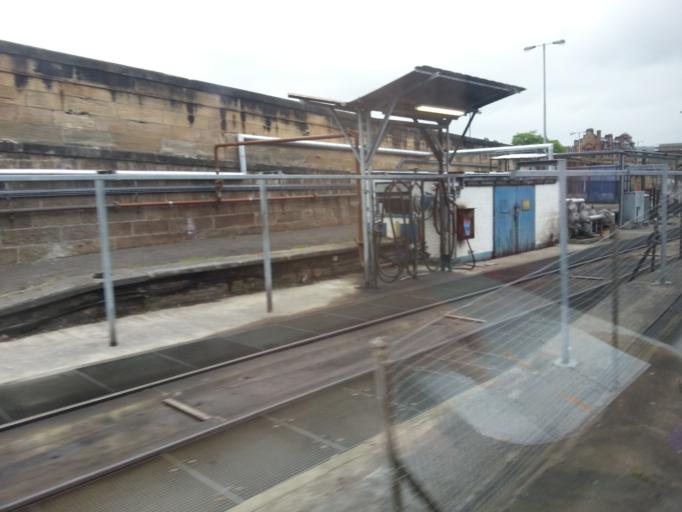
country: GB
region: Scotland
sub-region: Perth and Kinross
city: Perth
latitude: 56.3941
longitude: -3.4413
